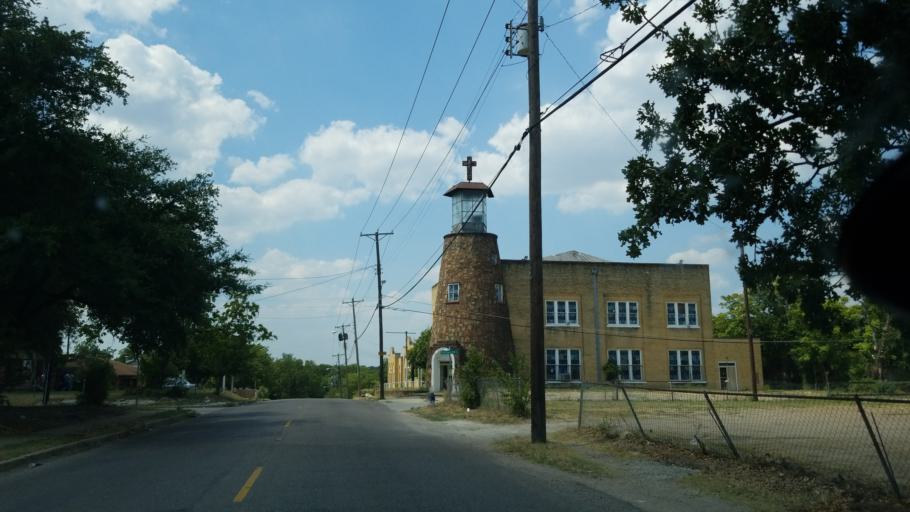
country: US
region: Texas
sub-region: Dallas County
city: Dallas
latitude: 32.7392
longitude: -96.8088
